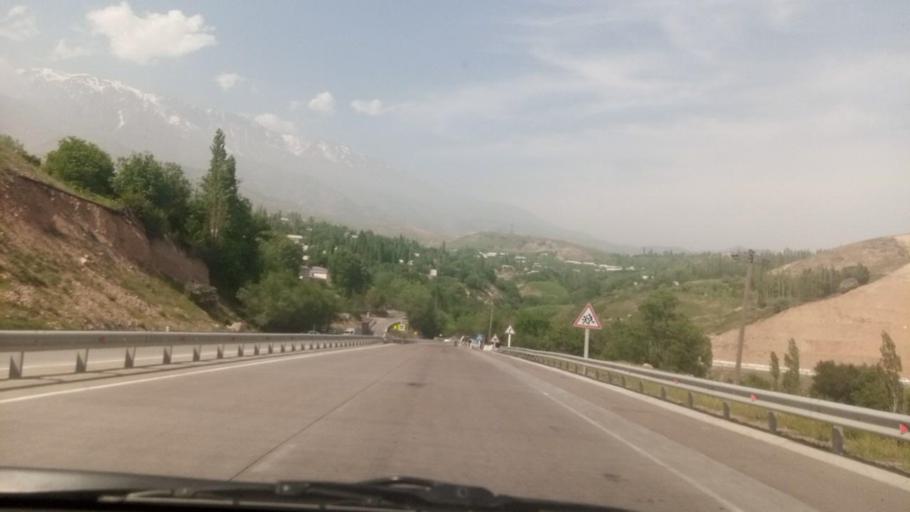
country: UZ
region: Toshkent
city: Angren
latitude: 41.0709
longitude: 70.2330
